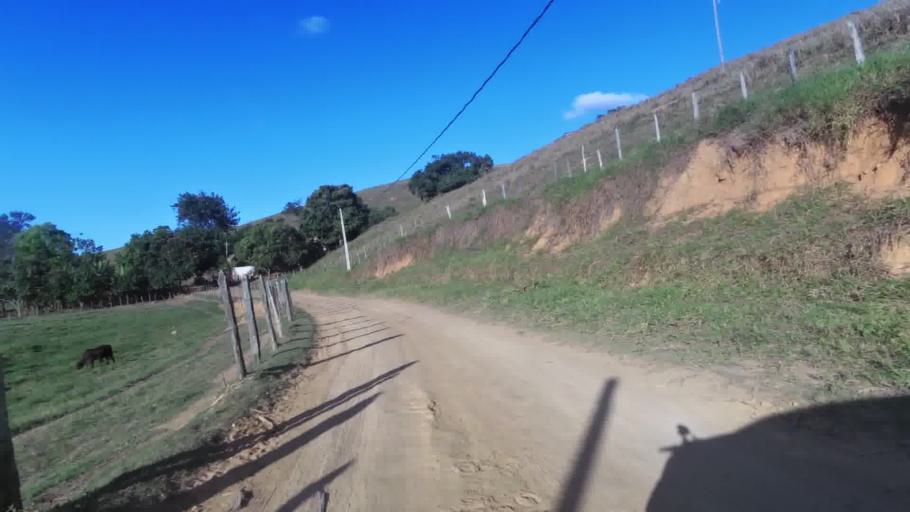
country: BR
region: Espirito Santo
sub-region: Marataizes
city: Marataizes
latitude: -21.1482
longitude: -41.0313
